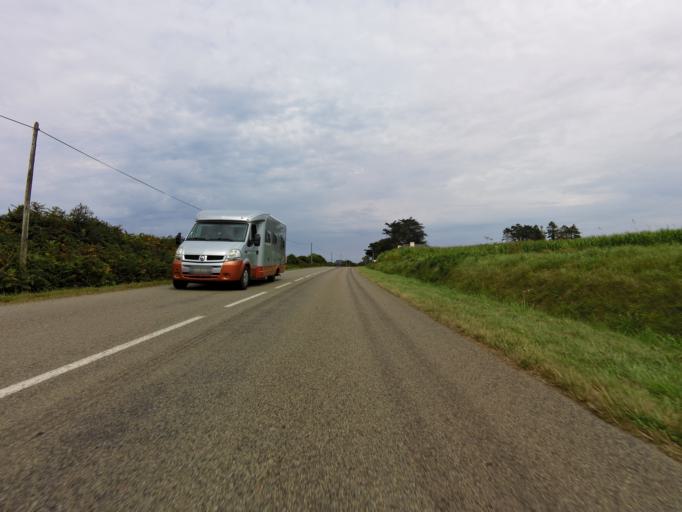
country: FR
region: Brittany
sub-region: Departement du Finistere
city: Poullan-sur-Mer
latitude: 48.0807
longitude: -4.4369
